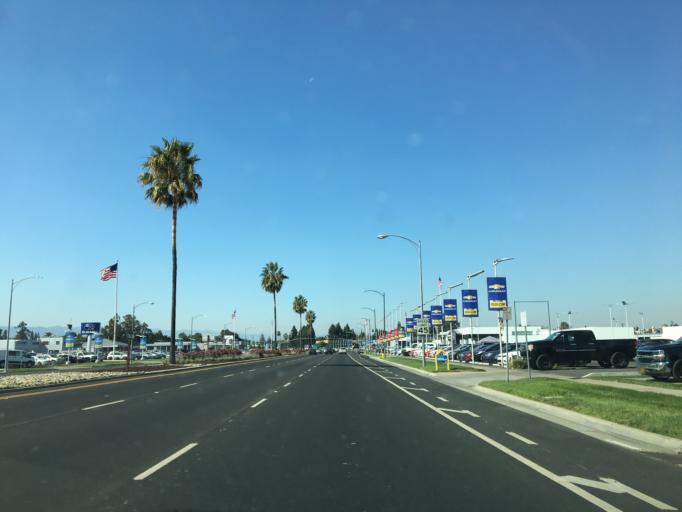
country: US
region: California
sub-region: Santa Clara County
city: Seven Trees
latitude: 37.2755
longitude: -121.8713
